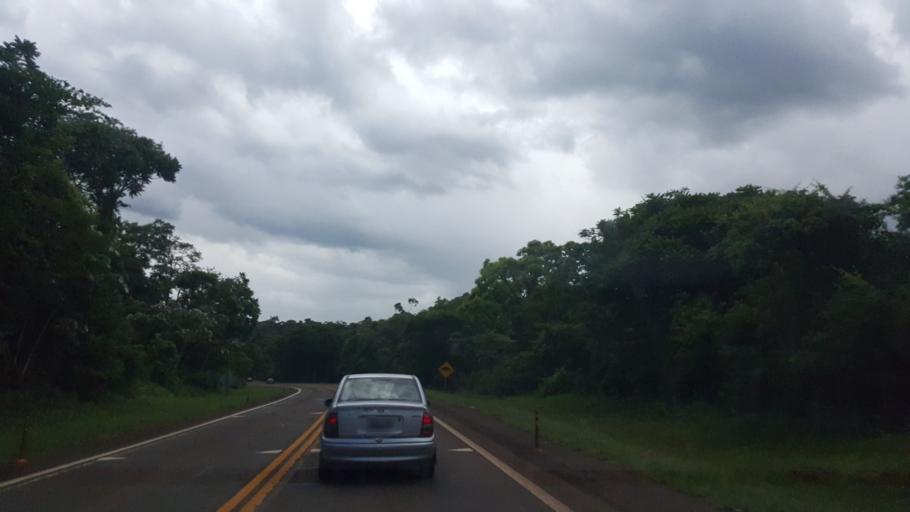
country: AR
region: Misiones
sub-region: Departamento de Iguazu
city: Puerto Iguazu
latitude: -25.7299
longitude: -54.5316
